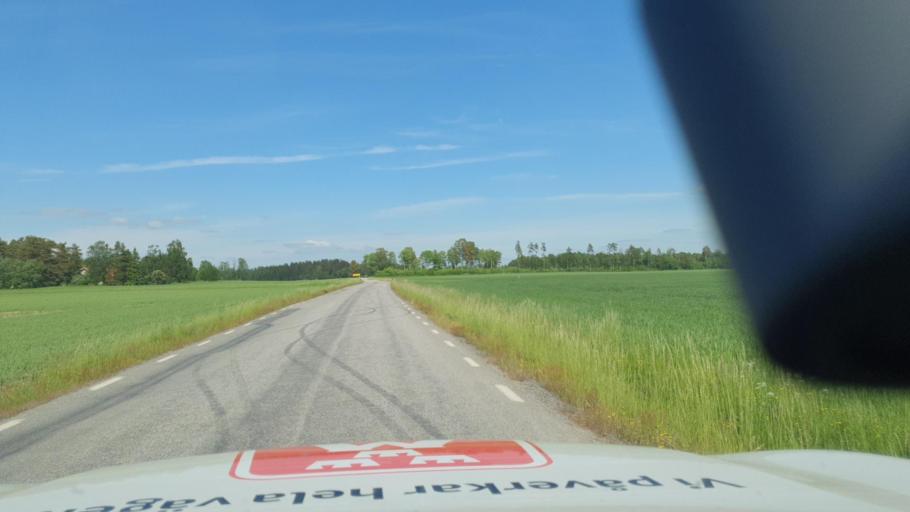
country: SE
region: Vaestra Goetaland
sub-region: Essunga Kommun
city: Nossebro
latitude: 58.2572
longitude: 12.7224
